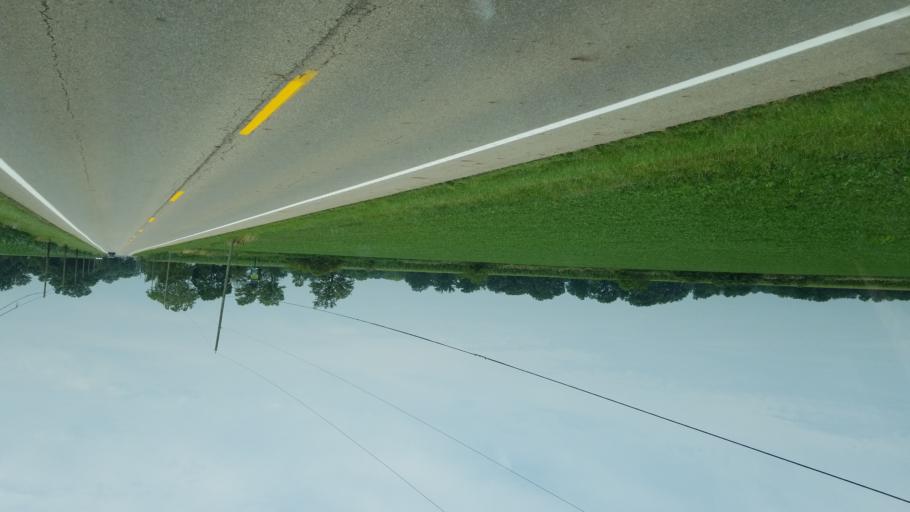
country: US
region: Ohio
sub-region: Madison County
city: Plain City
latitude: 40.0941
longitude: -83.2809
